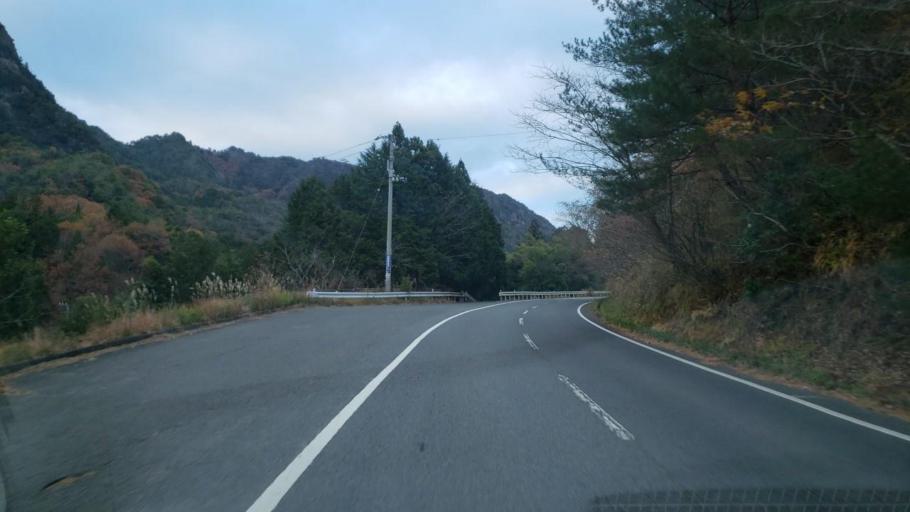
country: JP
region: Tokushima
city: Wakimachi
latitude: 34.1843
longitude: 134.1987
